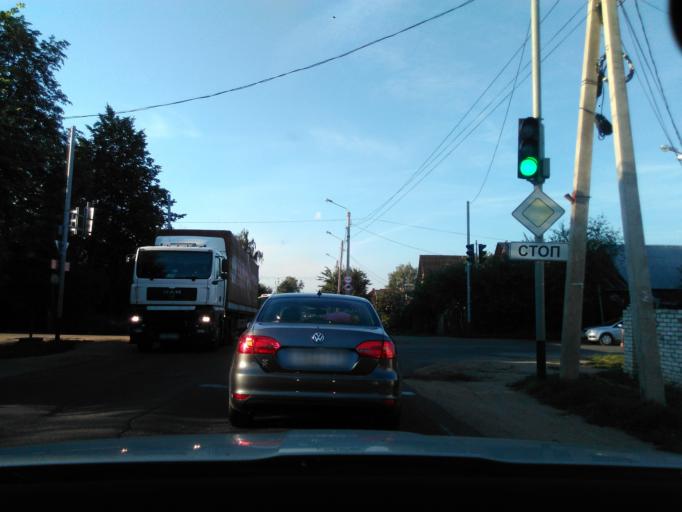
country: RU
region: Tverskaya
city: Konakovo
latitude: 56.7018
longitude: 36.7680
